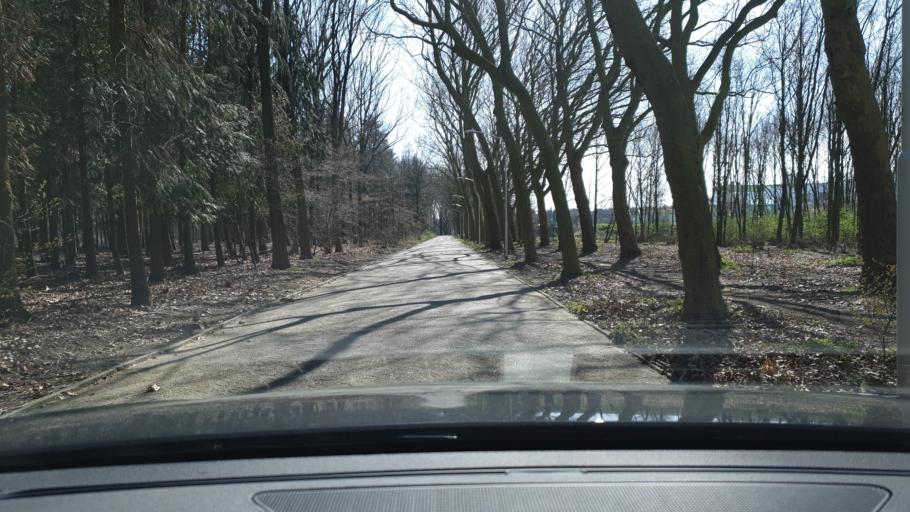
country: NL
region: North Brabant
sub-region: Gemeente Best
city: Best
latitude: 51.4912
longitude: 5.3992
